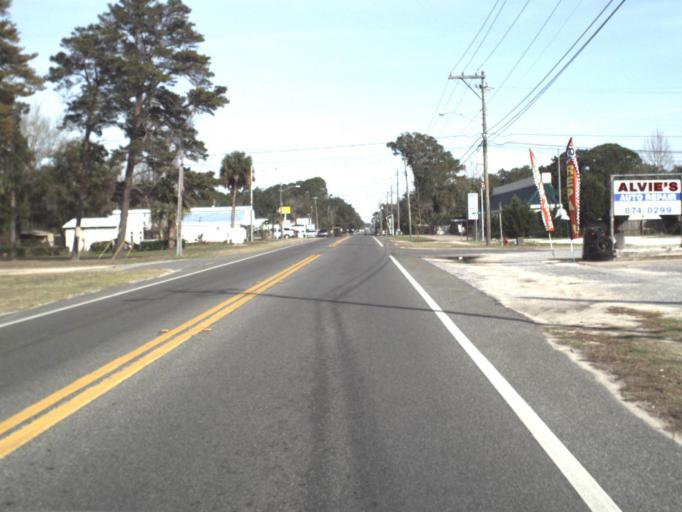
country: US
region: Florida
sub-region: Bay County
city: Parker
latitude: 30.1311
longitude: -85.6047
